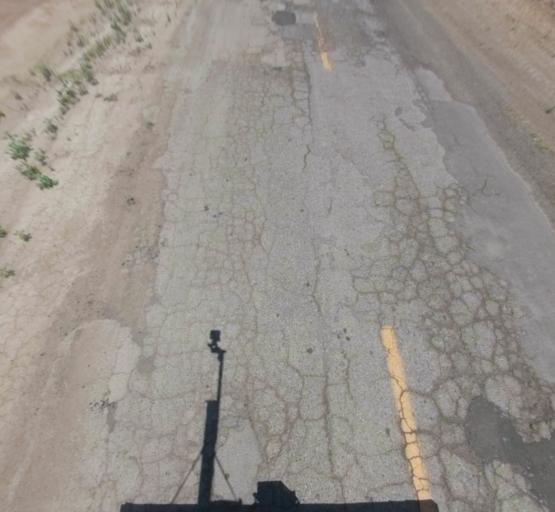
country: US
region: California
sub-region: Madera County
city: Chowchilla
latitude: 37.1152
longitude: -120.3652
